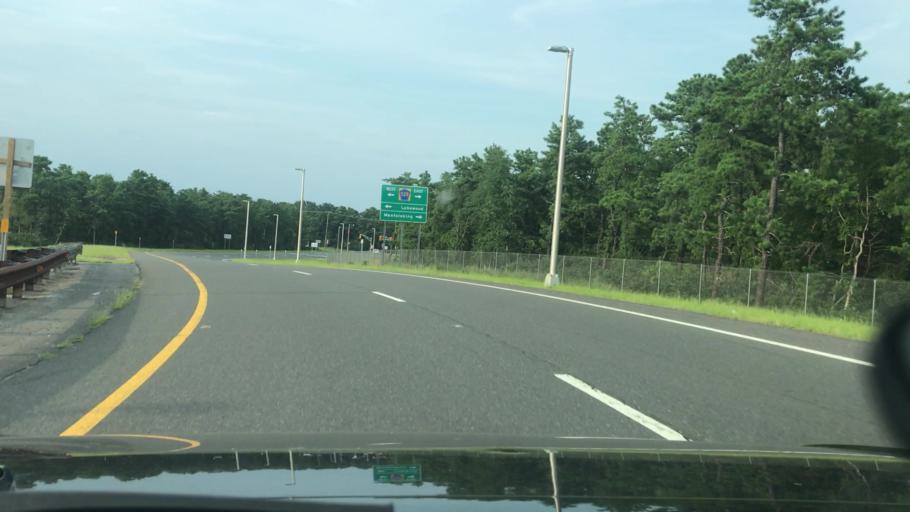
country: US
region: New Jersey
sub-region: Ocean County
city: Leisure Village
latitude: 40.0618
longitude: -74.1612
